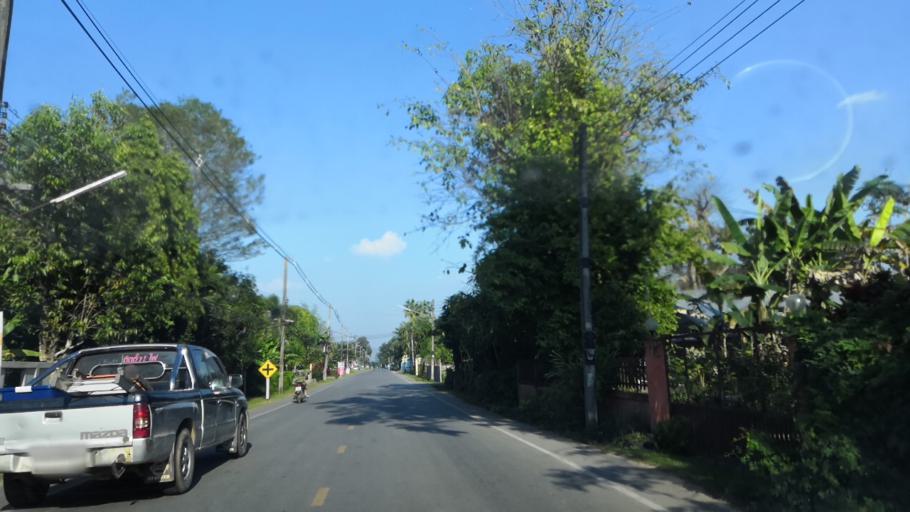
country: TH
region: Chiang Rai
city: Wiang Chai
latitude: 19.9370
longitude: 99.9075
